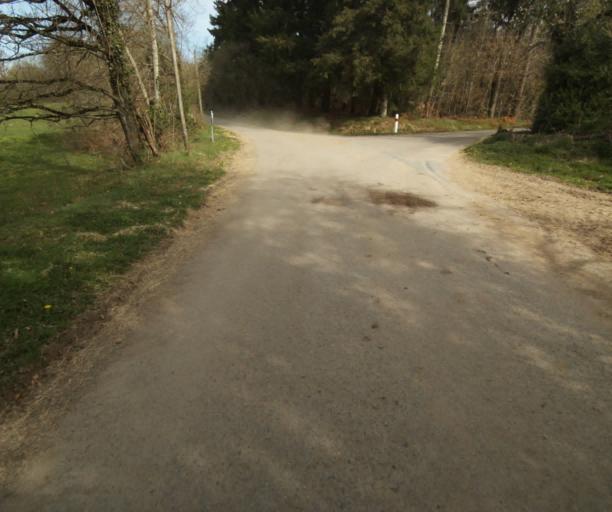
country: FR
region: Limousin
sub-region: Departement de la Correze
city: Correze
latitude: 45.3823
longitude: 1.8224
